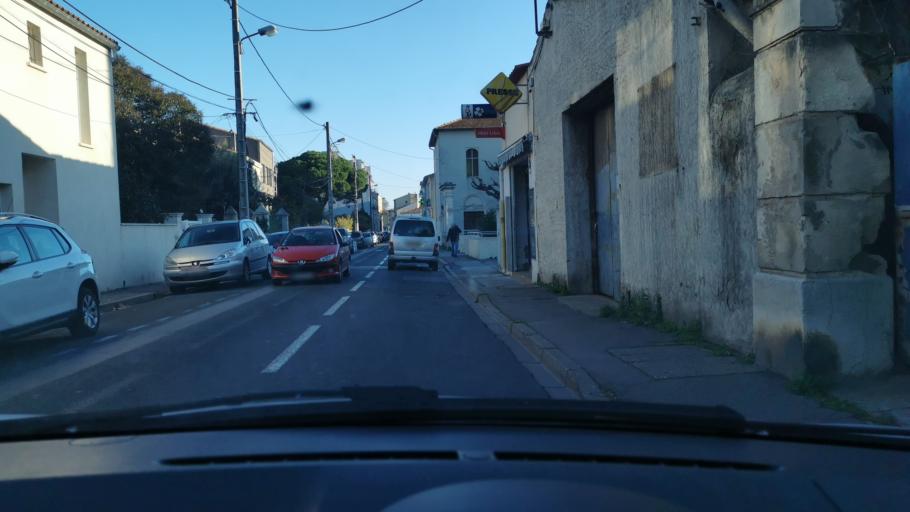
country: FR
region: Languedoc-Roussillon
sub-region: Departement de l'Herault
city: Frontignan
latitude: 43.4482
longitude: 3.7521
